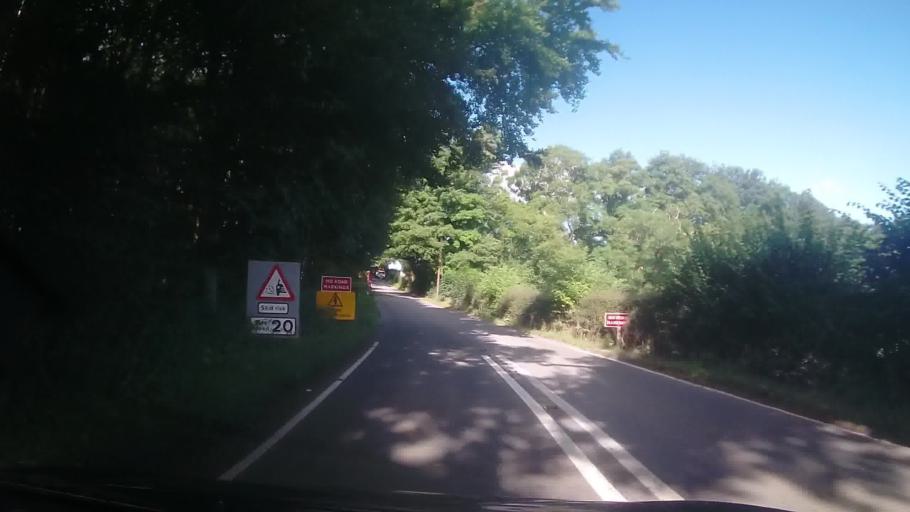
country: GB
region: England
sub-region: Shropshire
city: Bicton
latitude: 52.7616
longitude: -2.7915
